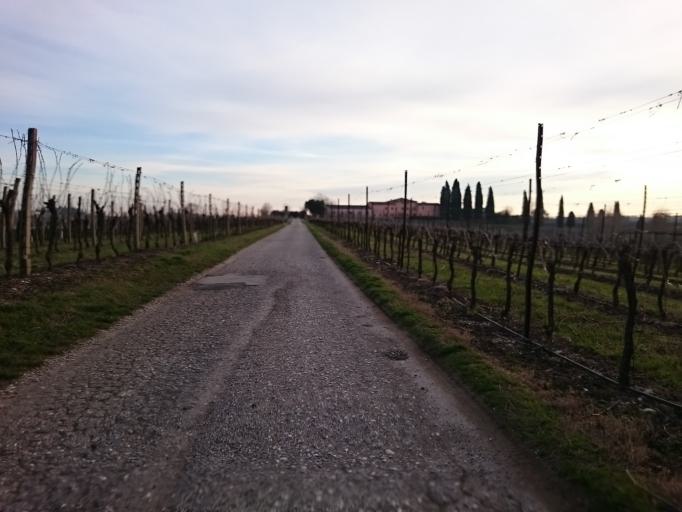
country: IT
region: Veneto
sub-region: Provincia di Verona
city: Castelnuovo del Garda
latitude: 45.4575
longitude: 10.7583
